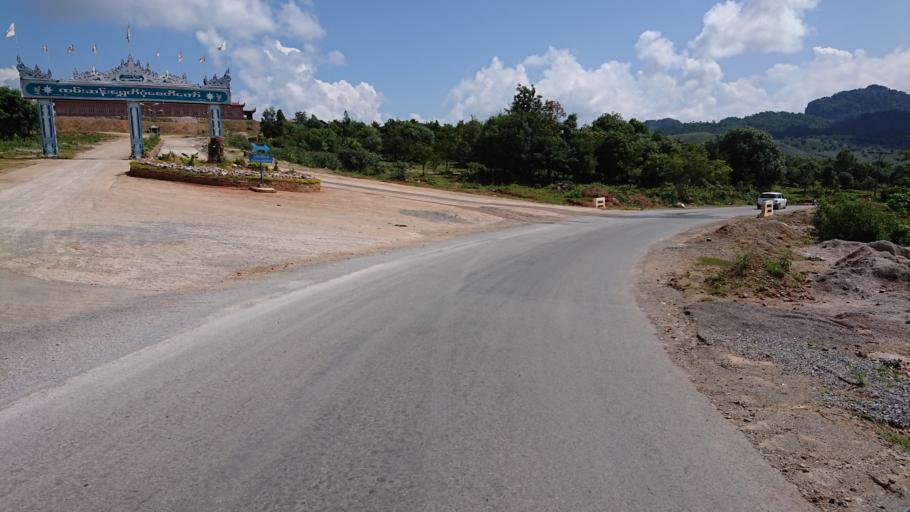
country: MM
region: Shan
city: Taunggyi
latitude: 20.8152
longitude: 97.3268
